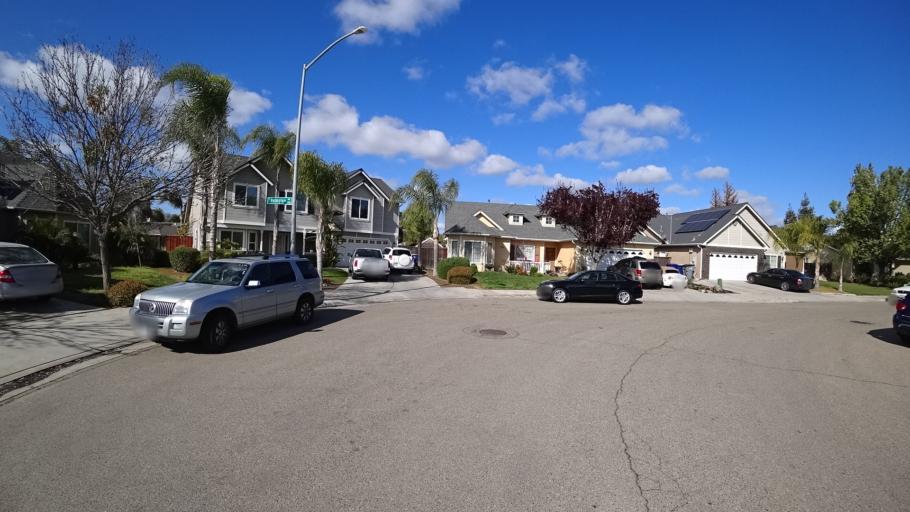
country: US
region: California
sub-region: Fresno County
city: West Park
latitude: 36.8285
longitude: -119.8766
